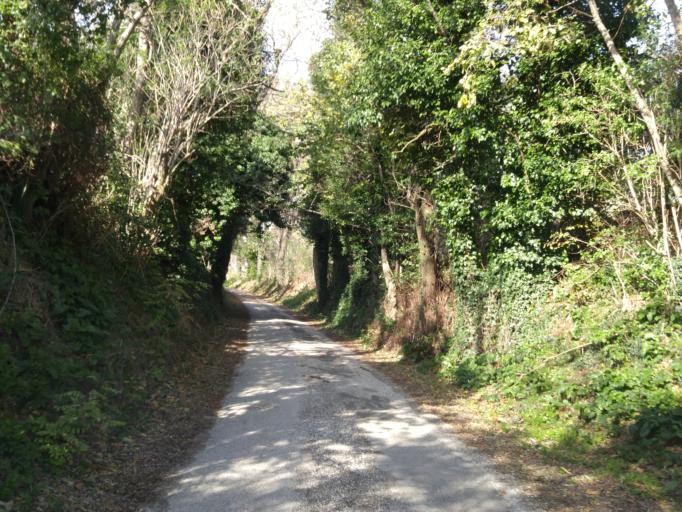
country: IT
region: The Marches
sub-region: Provincia di Pesaro e Urbino
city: Saltara
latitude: 43.7655
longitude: 12.9042
